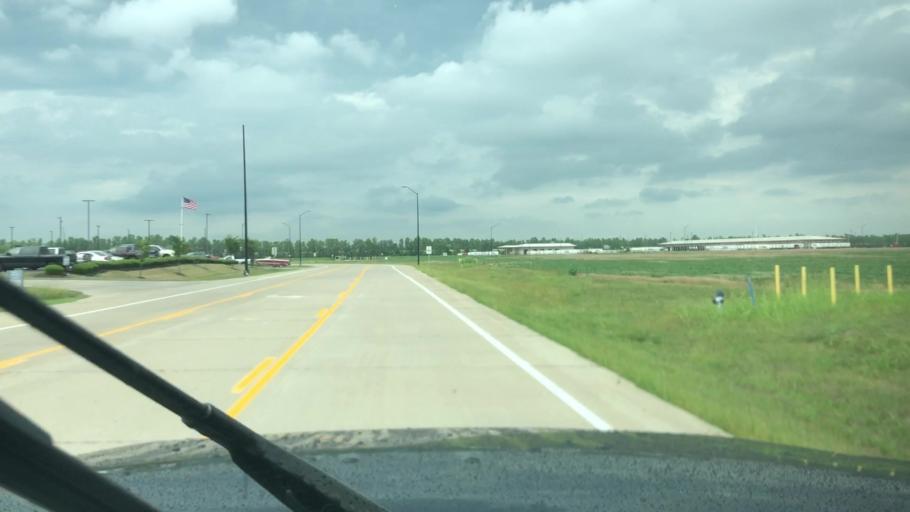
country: US
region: Missouri
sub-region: Saint Charles County
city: Saint Peters
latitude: 38.8062
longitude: -90.5808
